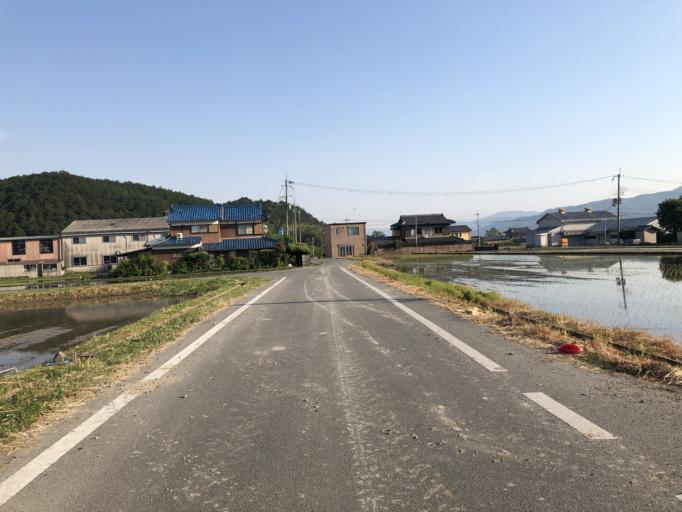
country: JP
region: Kyoto
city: Kameoka
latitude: 35.0728
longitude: 135.5568
